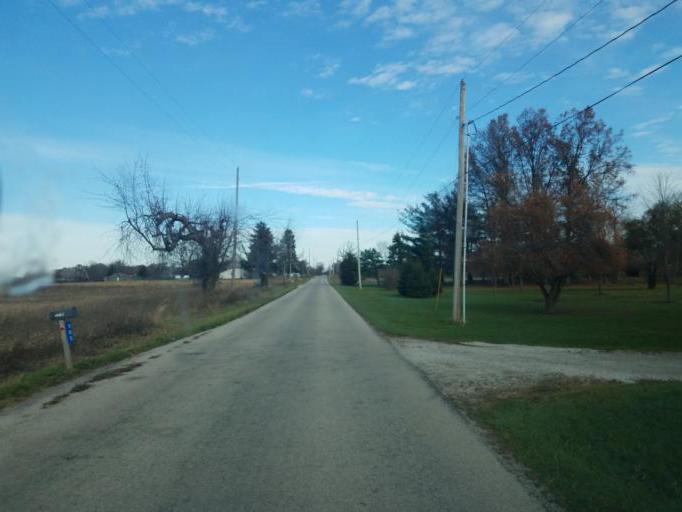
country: US
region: Ohio
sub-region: Crawford County
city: Galion
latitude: 40.7225
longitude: -82.7459
